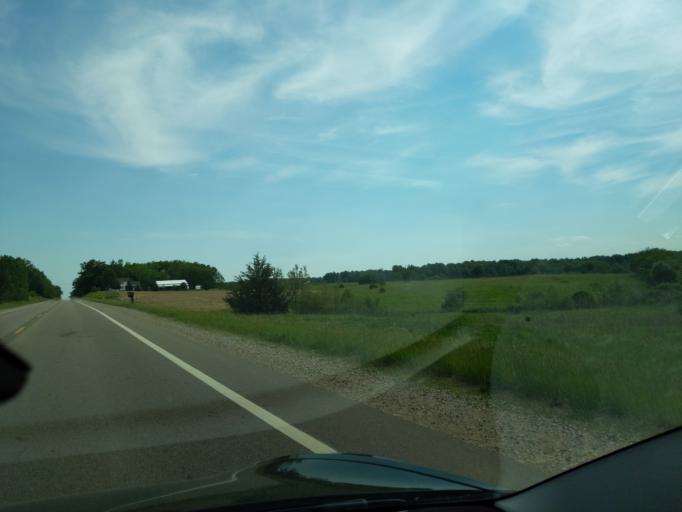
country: US
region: Michigan
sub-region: Barry County
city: Nashville
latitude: 42.6792
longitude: -85.0954
